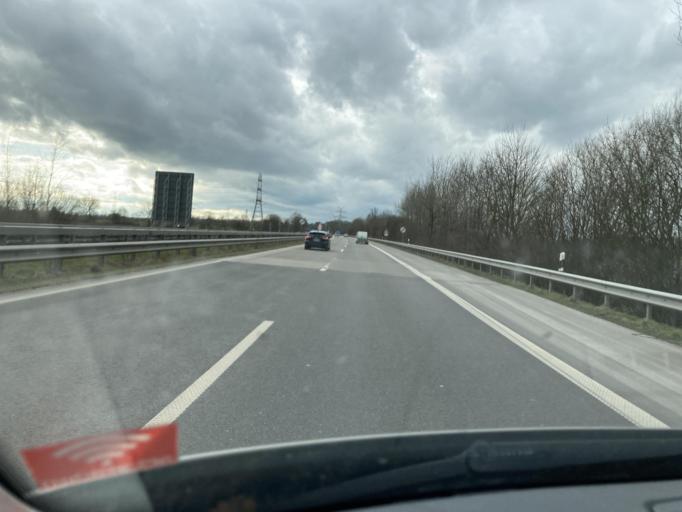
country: DE
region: Lower Saxony
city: Fedderwarden
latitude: 53.5572
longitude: 8.0720
